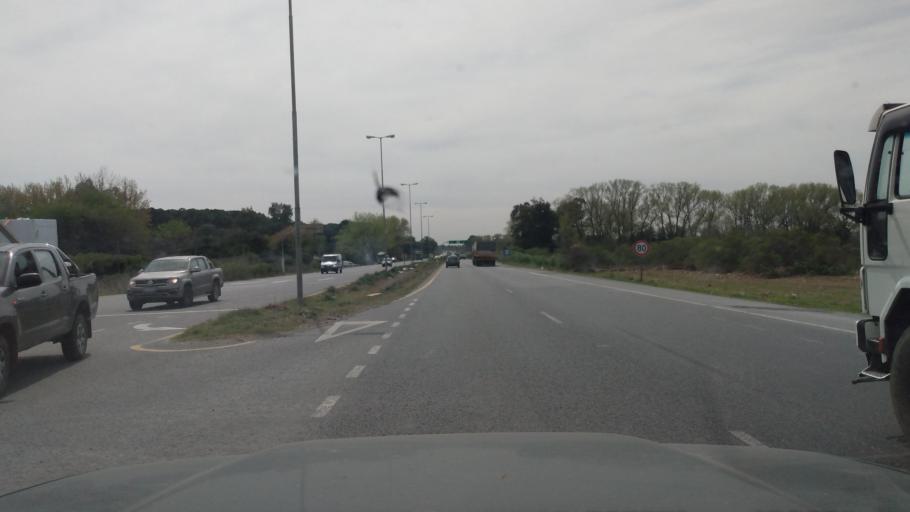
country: AR
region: Buenos Aires
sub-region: Partido de Lujan
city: Lujan
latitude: -34.4668
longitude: -59.0655
